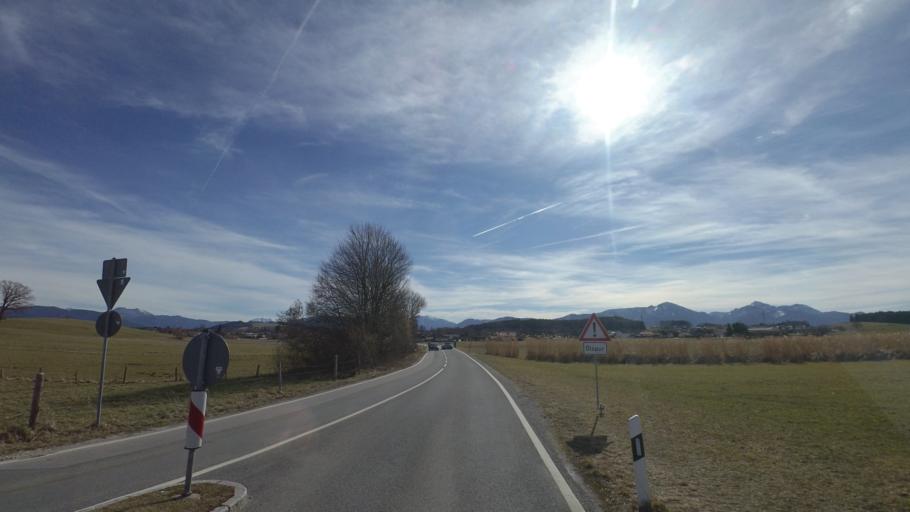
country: DE
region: Bavaria
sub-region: Upper Bavaria
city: Traunstein
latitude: 47.8762
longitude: 12.6208
